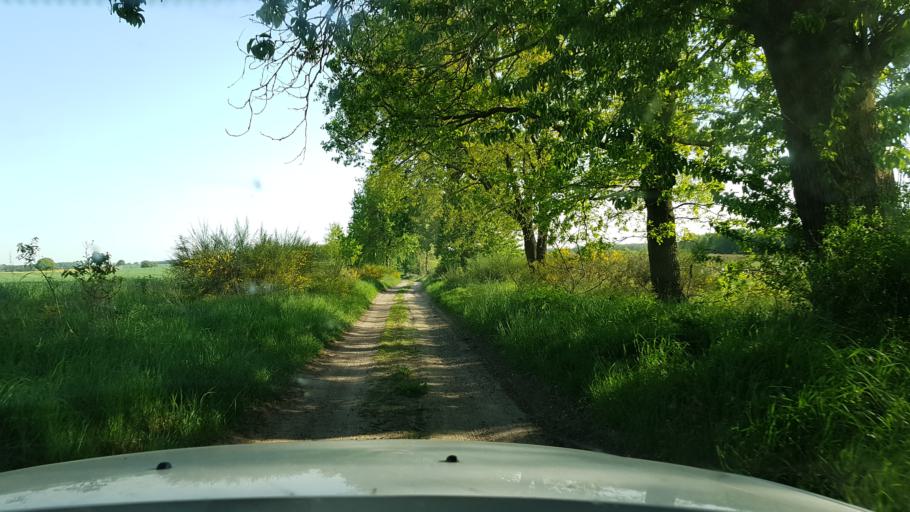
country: PL
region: West Pomeranian Voivodeship
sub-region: Powiat lobeski
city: Resko
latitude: 53.6990
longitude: 15.3364
